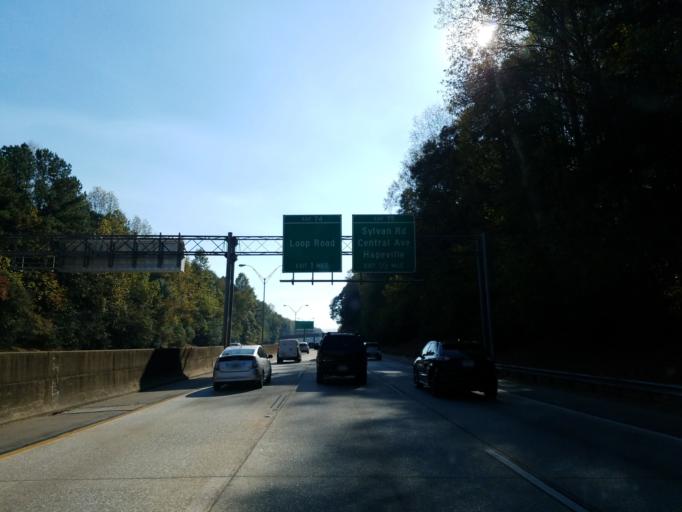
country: US
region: Georgia
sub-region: Fulton County
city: Hapeville
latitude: 33.6752
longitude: -84.4136
